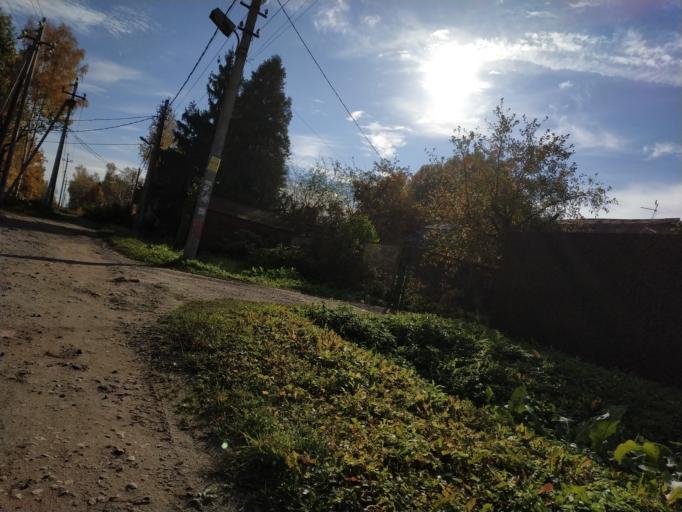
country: RU
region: Moskovskaya
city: Sheremet'yevskiy
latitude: 55.9844
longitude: 37.4965
